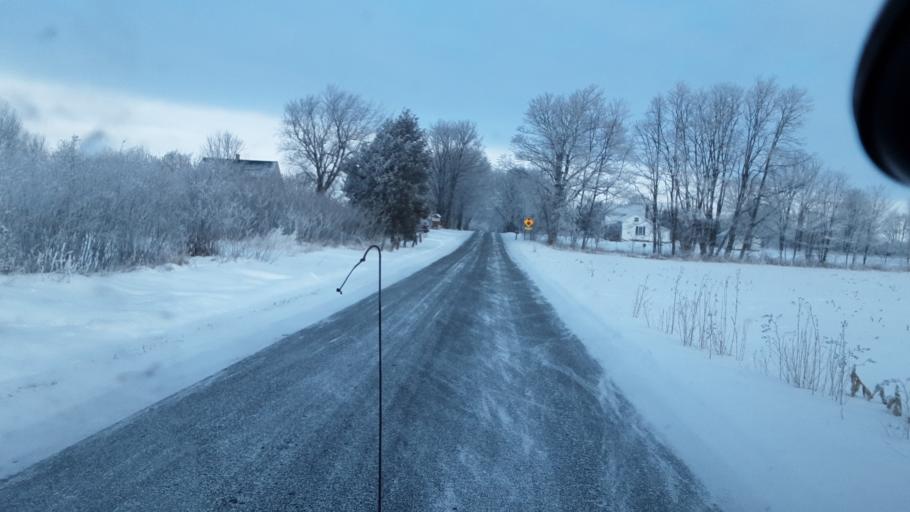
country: US
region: Michigan
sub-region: Ingham County
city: Leslie
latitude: 42.4338
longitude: -84.4970
